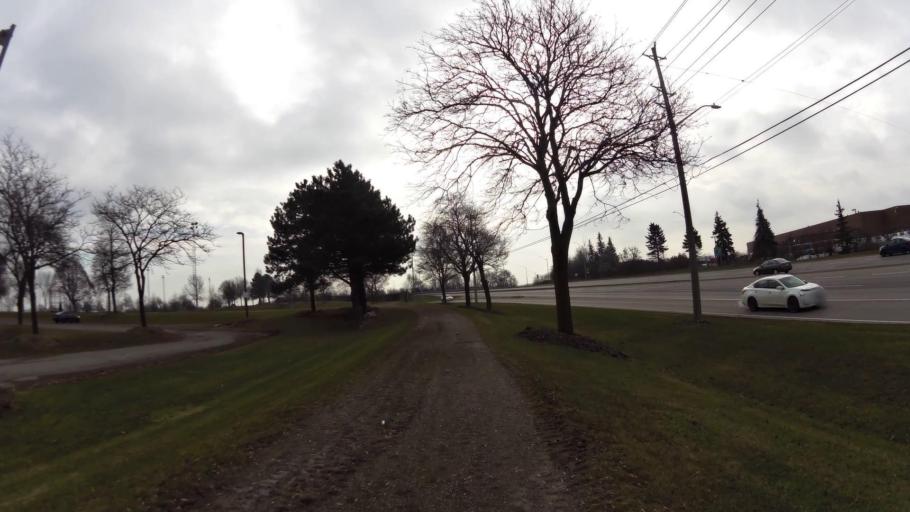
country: CA
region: Ontario
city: Kitchener
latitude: 43.4010
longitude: -80.4561
